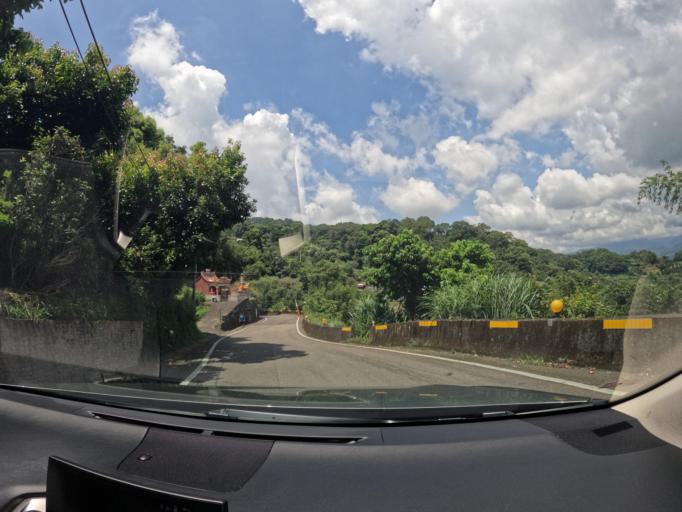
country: TW
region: Taiwan
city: Fengyuan
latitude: 24.3811
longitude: 120.8259
